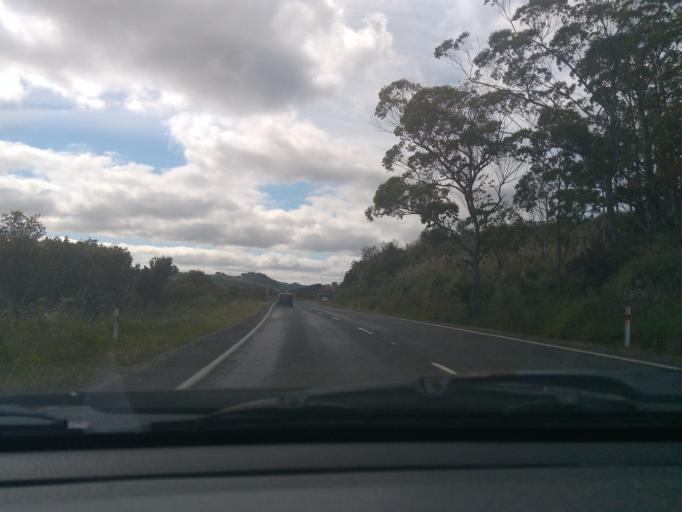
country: NZ
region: Northland
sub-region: Far North District
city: Taipa
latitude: -35.0088
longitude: 173.5405
